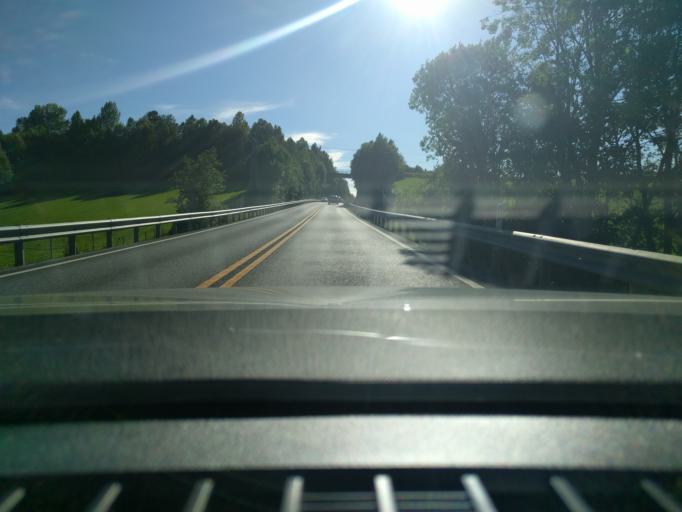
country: NO
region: Buskerud
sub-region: Royken
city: Royken
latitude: 59.7411
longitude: 10.3981
